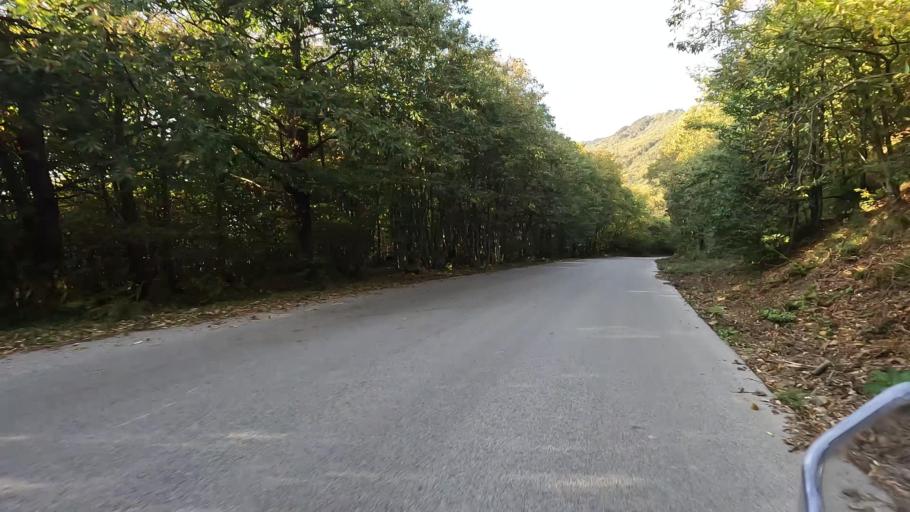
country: IT
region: Liguria
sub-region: Provincia di Savona
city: San Giovanni
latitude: 44.4122
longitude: 8.5271
